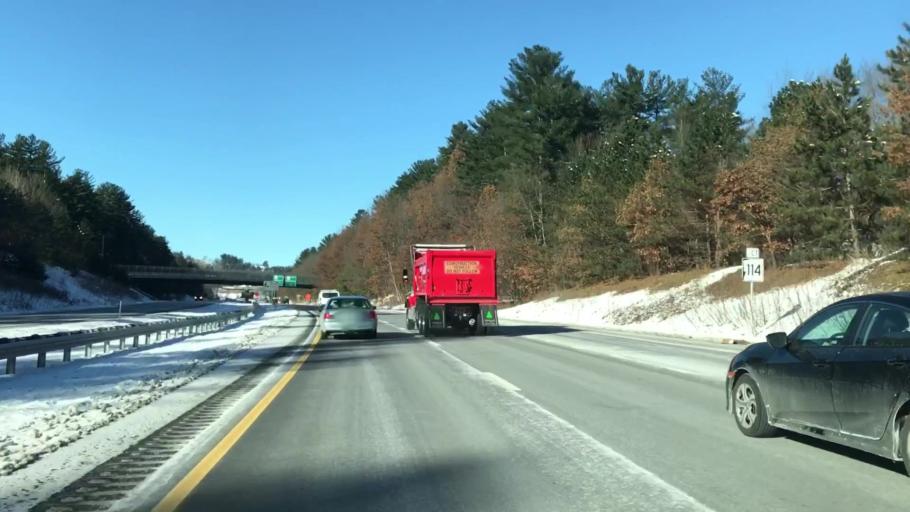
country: US
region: New Hampshire
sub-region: Hillsborough County
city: Bedford
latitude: 42.9579
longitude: -71.4908
